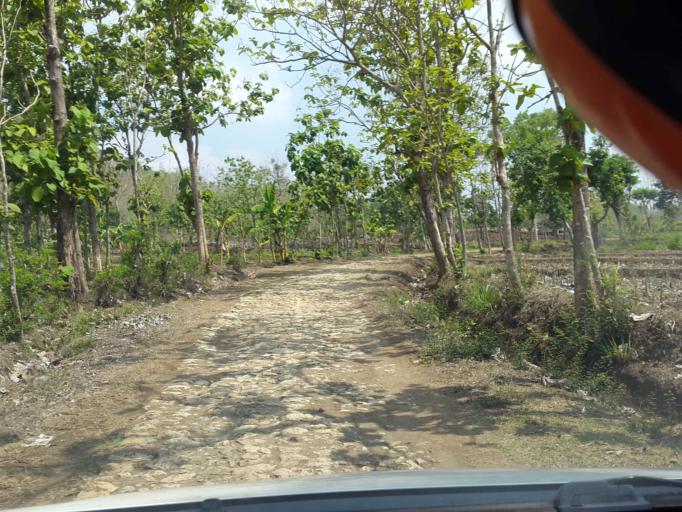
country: ID
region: East Java
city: Ponorogo
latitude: -7.8155
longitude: 111.3191
